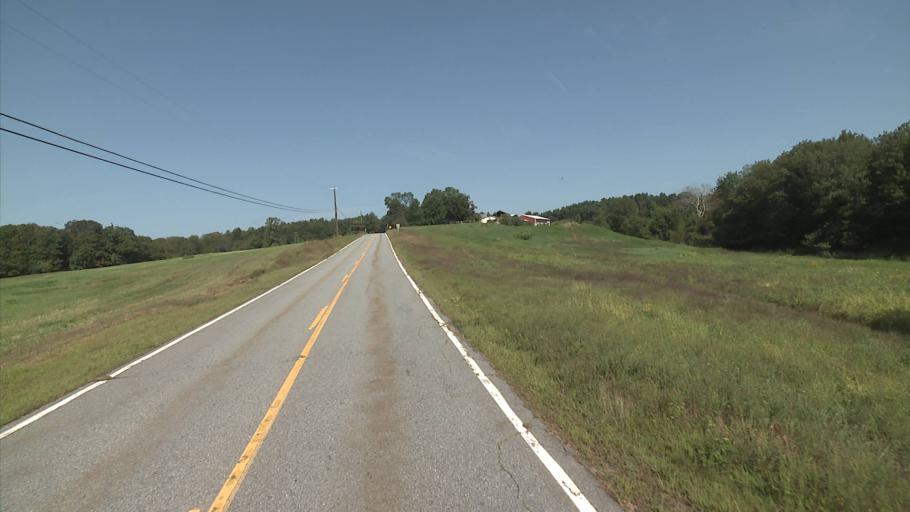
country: US
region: Connecticut
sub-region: Windham County
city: Quinebaug
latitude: 42.0151
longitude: -72.0051
